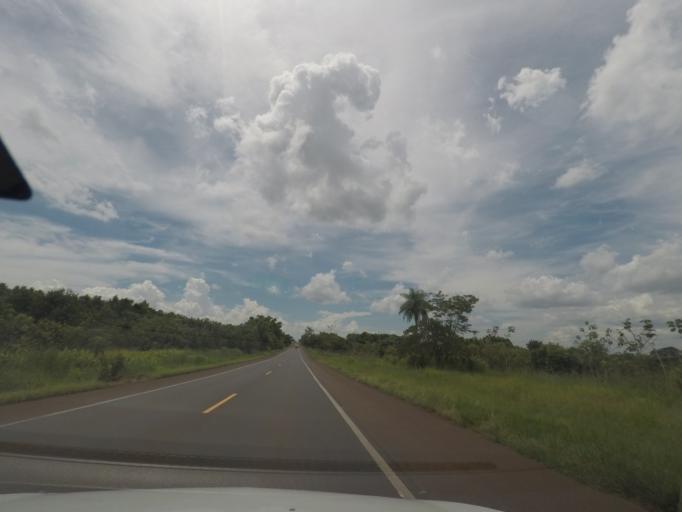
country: BR
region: Sao Paulo
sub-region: Barretos
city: Barretos
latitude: -20.3702
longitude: -48.6457
